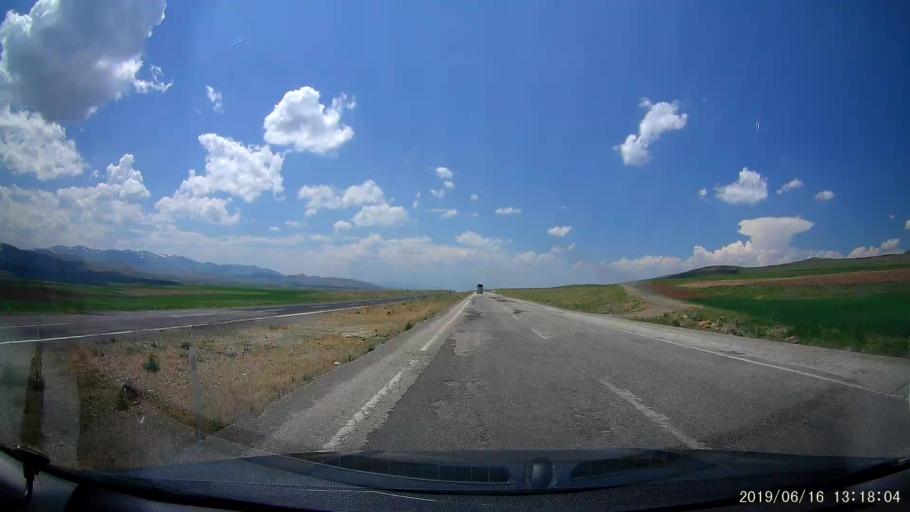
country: TR
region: Agri
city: Taslicay
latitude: 39.6291
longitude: 43.4392
